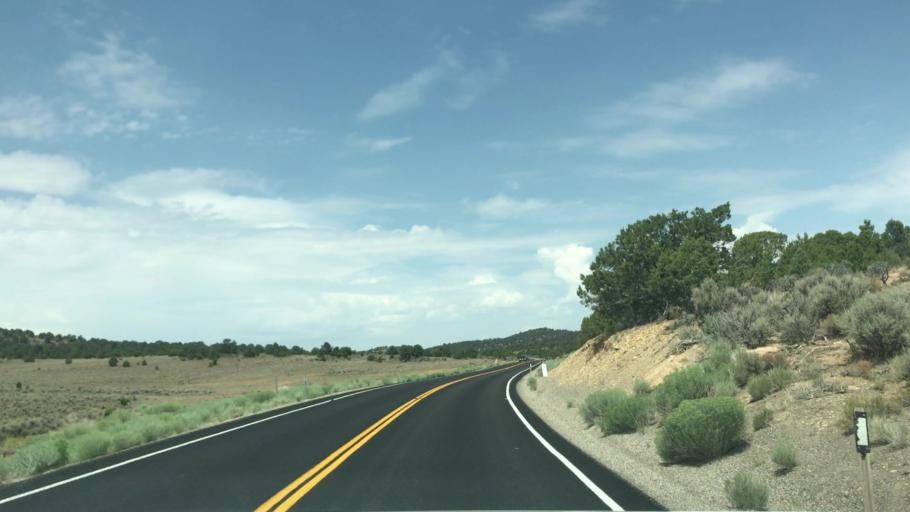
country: US
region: Nevada
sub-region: Eureka County
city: Eureka
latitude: 39.3921
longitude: -115.4565
